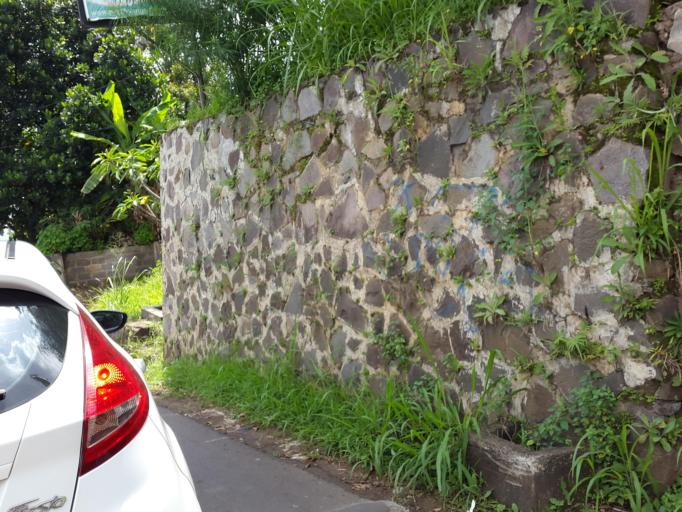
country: ID
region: West Java
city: Bandung
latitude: -6.8881
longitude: 107.6666
